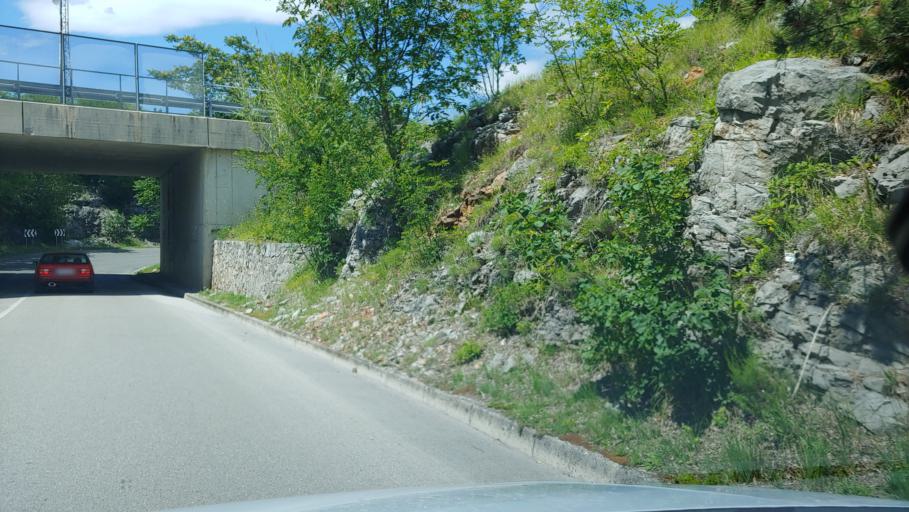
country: SI
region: Sezana
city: Sezana
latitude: 45.7020
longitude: 13.8444
